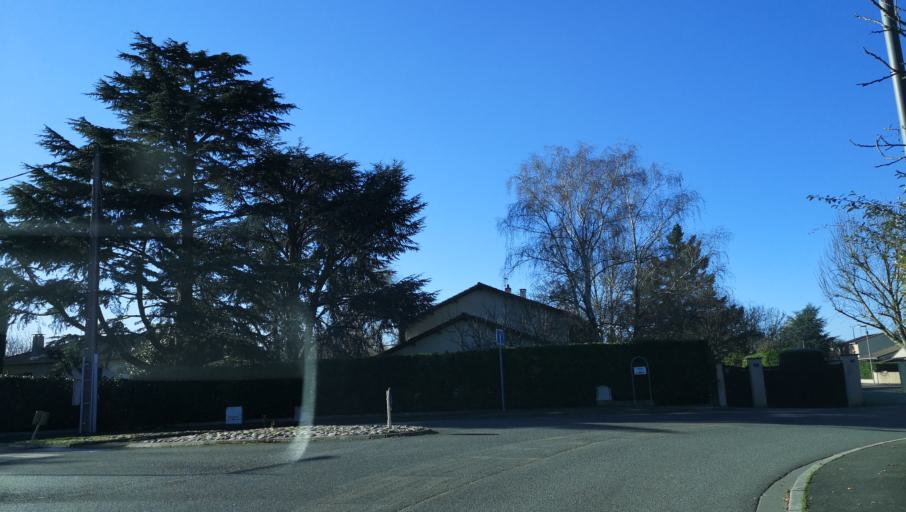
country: FR
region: Midi-Pyrenees
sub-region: Departement de la Haute-Garonne
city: Beauzelle
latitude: 43.6624
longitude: 1.3883
